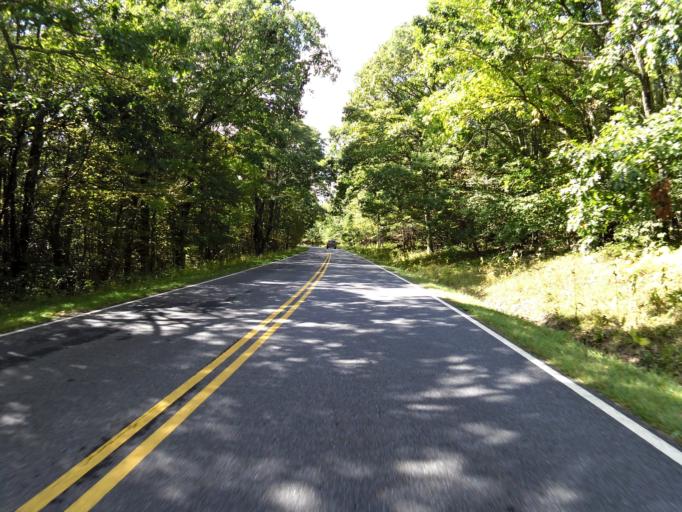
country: US
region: Virginia
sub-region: Page County
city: Stanley
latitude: 38.5446
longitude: -78.3972
